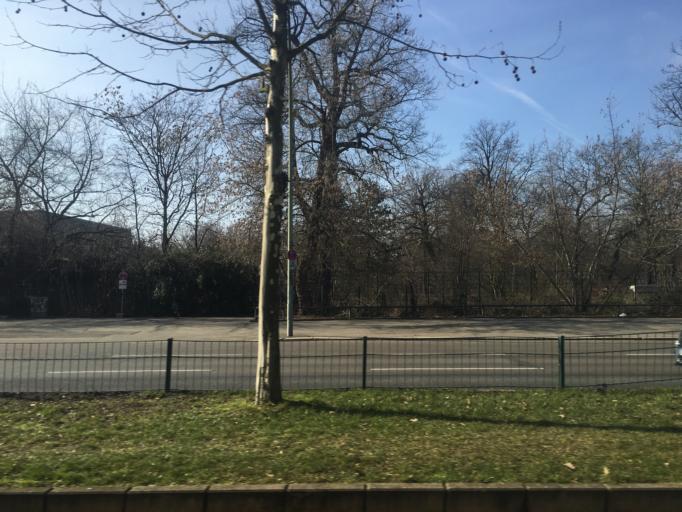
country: DE
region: Berlin
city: Friedrichshain Bezirk
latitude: 52.5280
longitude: 13.4459
